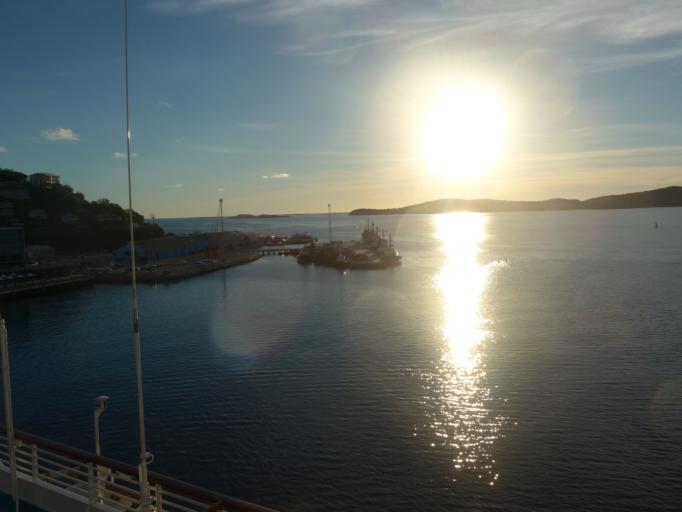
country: PG
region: National Capital
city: Port Moresby
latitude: -9.4763
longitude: 147.1454
